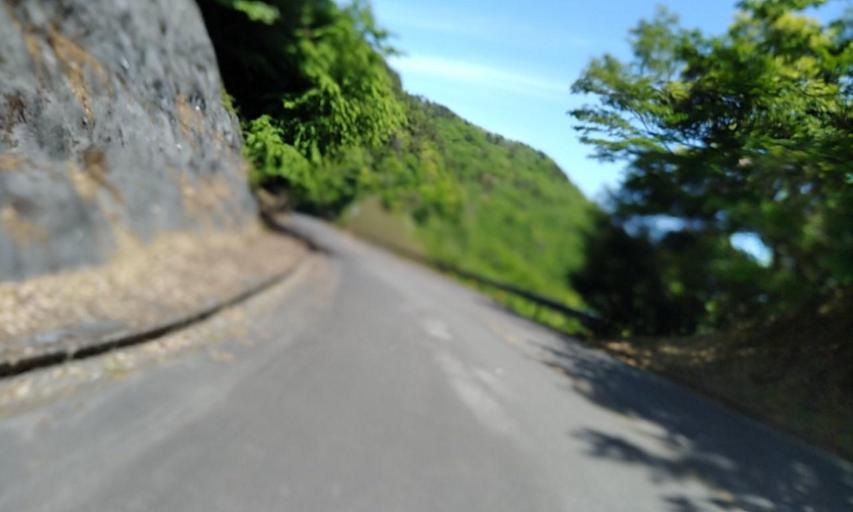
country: JP
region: Fukui
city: Obama
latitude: 35.5453
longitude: 135.7392
